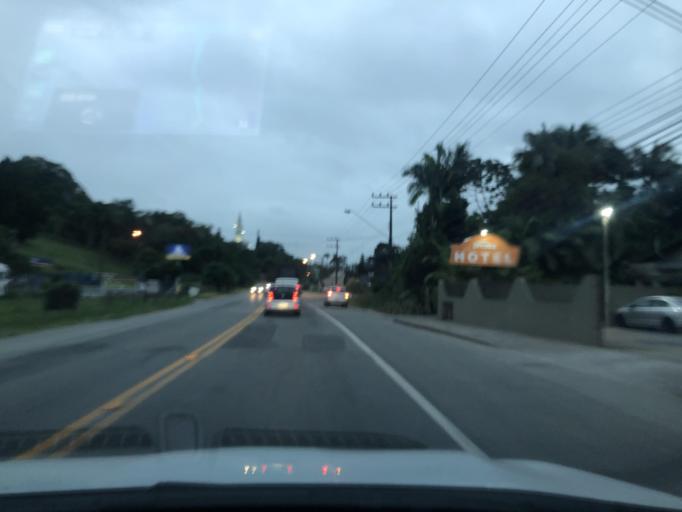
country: BR
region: Santa Catarina
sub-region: Pomerode
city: Pomerode
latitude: -26.7893
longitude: -49.0863
